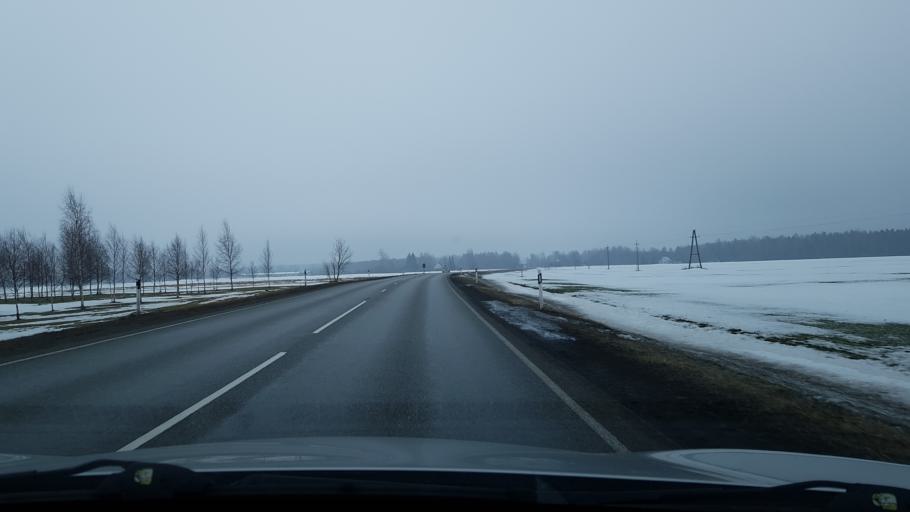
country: EE
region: Valgamaa
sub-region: Valga linn
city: Valga
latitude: 57.9196
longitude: 26.1824
